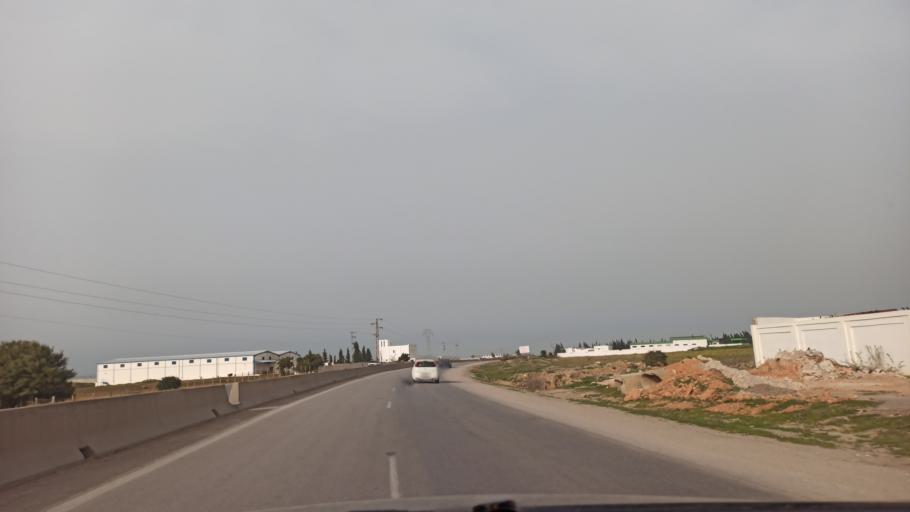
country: TN
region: Tunis
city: La Mohammedia
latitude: 36.5678
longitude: 10.0842
